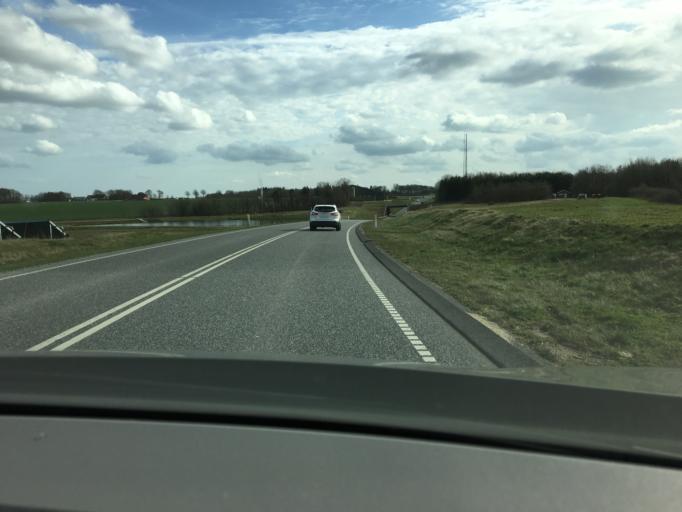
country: DK
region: South Denmark
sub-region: Vejle Kommune
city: Jelling
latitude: 55.7628
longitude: 9.4387
